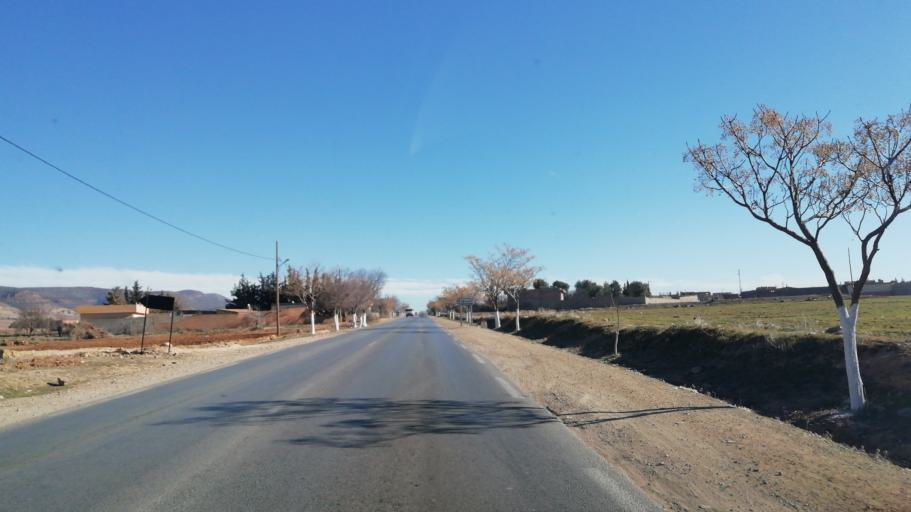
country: DZ
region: Tlemcen
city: Sebdou
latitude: 34.6629
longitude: -1.2922
